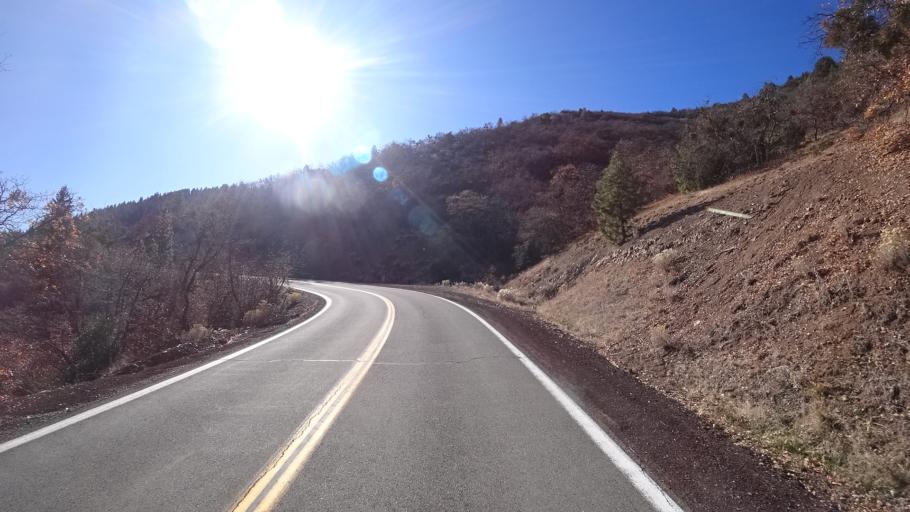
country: US
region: California
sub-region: Siskiyou County
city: Weed
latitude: 41.4484
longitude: -122.6472
